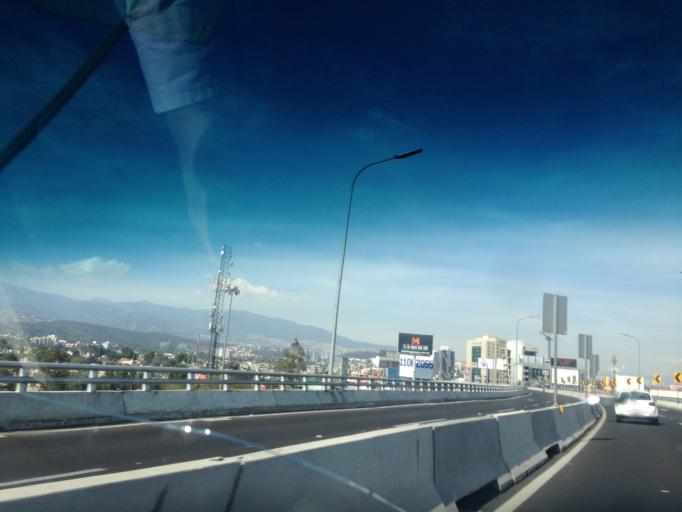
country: MX
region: Mexico City
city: Tlalpan
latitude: 19.3004
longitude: -99.1599
